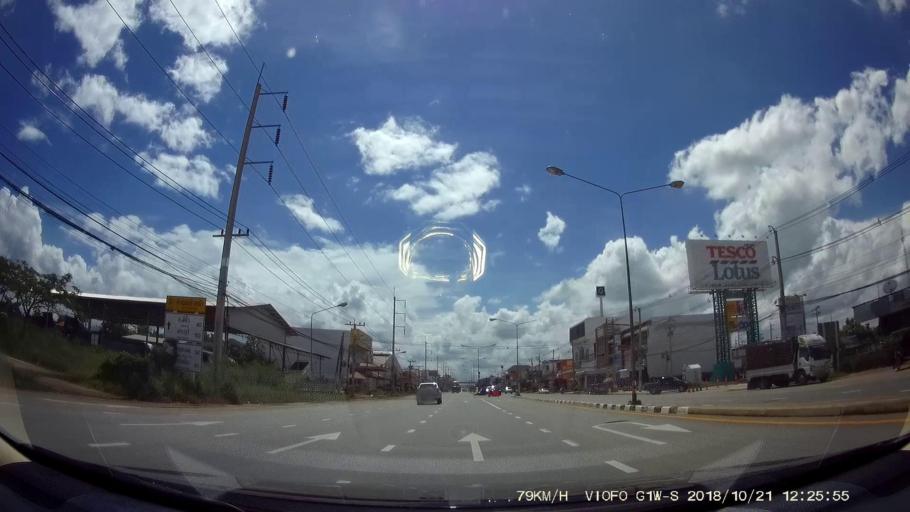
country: TH
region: Nakhon Ratchasima
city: Dan Khun Thot
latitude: 15.2153
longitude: 101.7696
